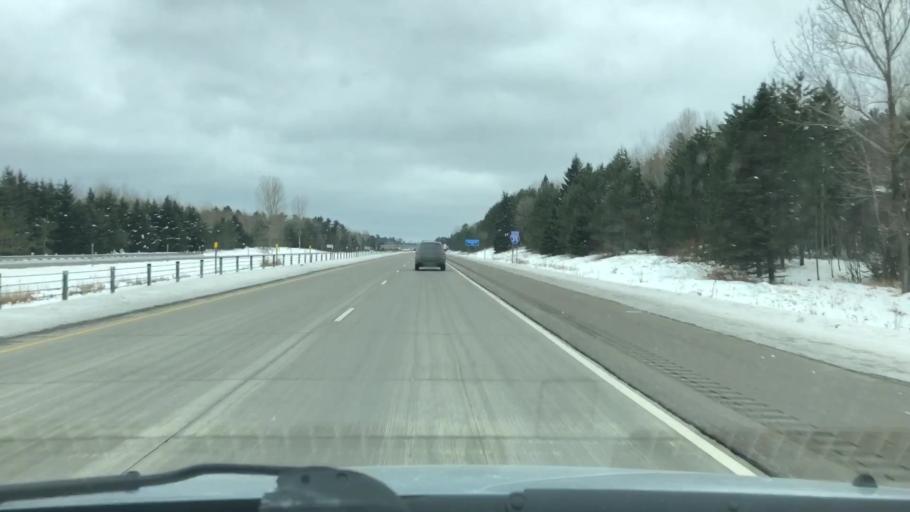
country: US
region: Minnesota
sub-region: Carlton County
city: Esko
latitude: 46.7019
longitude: -92.3111
